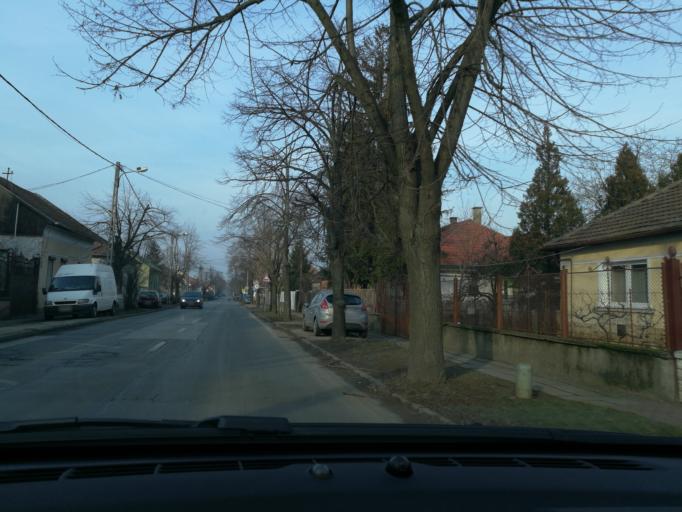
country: HU
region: Szabolcs-Szatmar-Bereg
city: Nyiregyhaza
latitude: 47.9518
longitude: 21.6943
